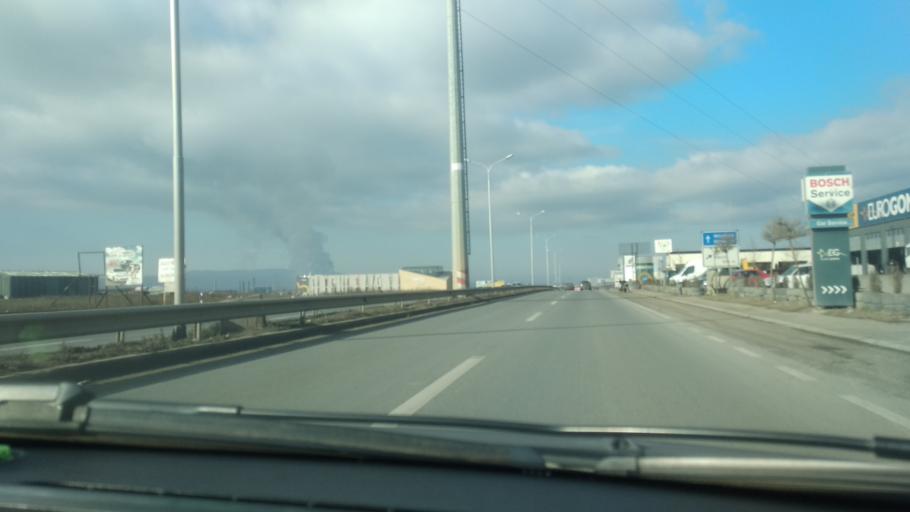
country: XK
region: Pristina
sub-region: Kosovo Polje
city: Kosovo Polje
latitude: 42.6630
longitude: 21.1293
